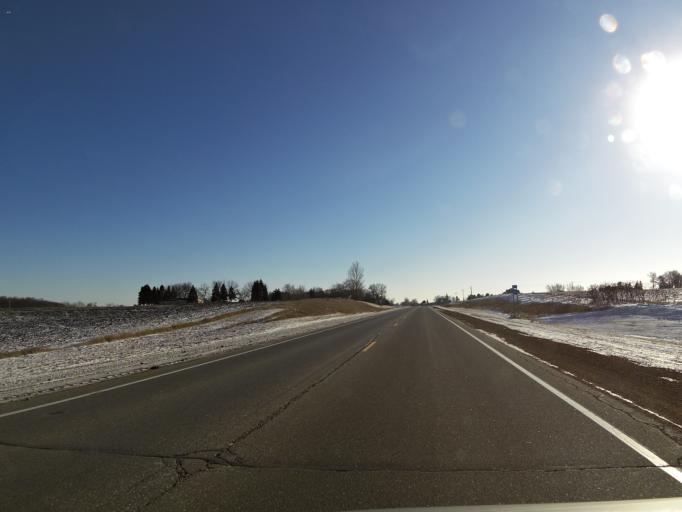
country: US
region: Minnesota
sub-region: Le Sueur County
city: New Prague
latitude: 44.6047
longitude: -93.5014
